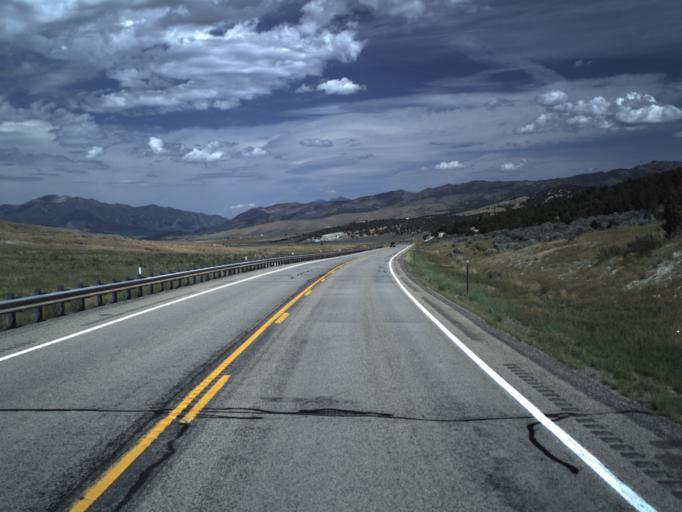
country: US
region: Utah
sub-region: Sanpete County
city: Fairview
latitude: 39.7349
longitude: -111.4770
